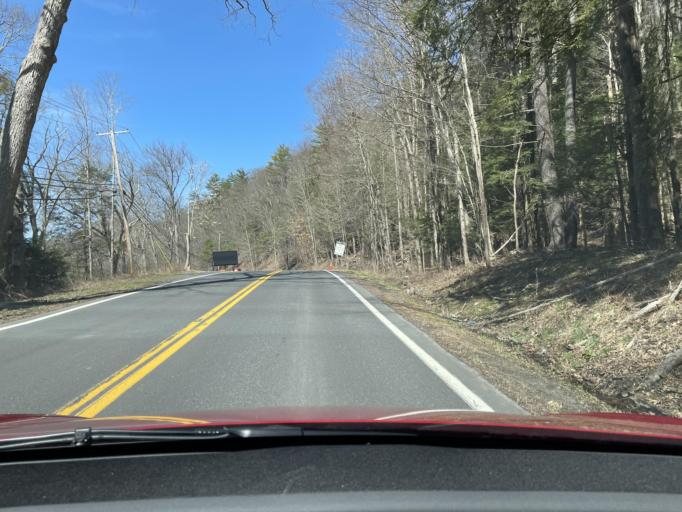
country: US
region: New York
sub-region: Ulster County
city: Lake Katrine
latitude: 41.9834
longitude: -74.0270
